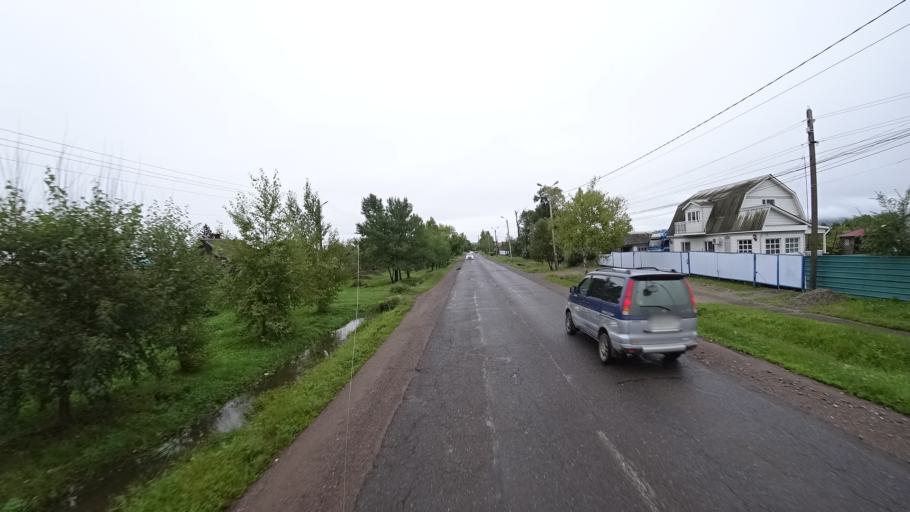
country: RU
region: Primorskiy
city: Monastyrishche
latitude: 44.1995
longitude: 132.4601
